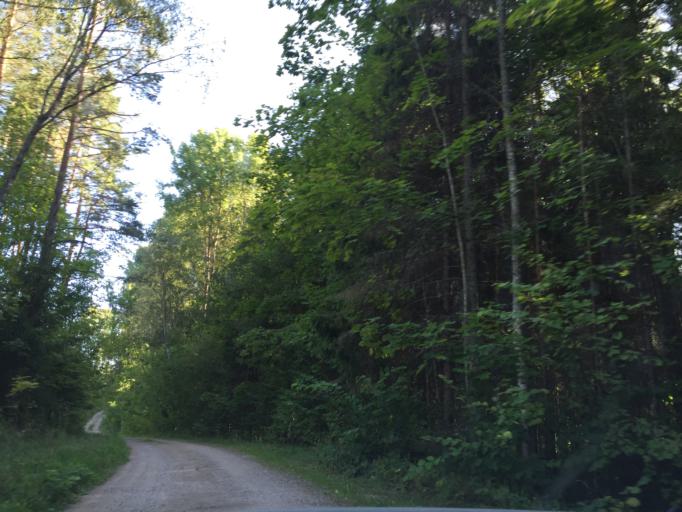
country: LT
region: Panevezys
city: Rokiskis
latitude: 55.8259
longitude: 25.8955
